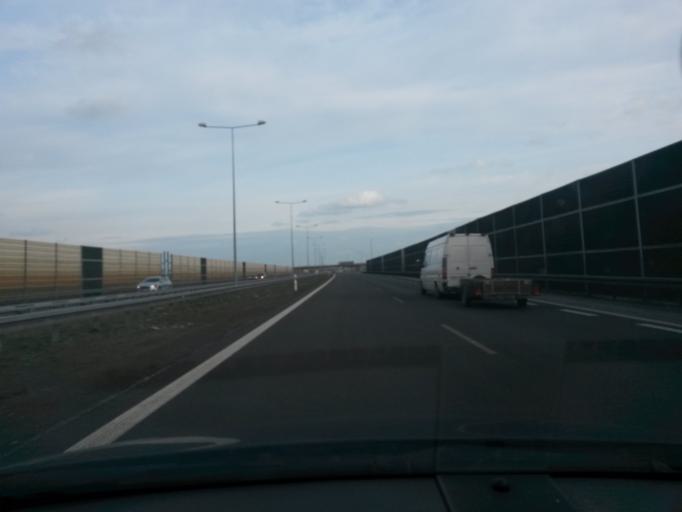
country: PL
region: Greater Poland Voivodeship
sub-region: Powiat kolski
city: Dabie
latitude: 52.0733
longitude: 18.8097
